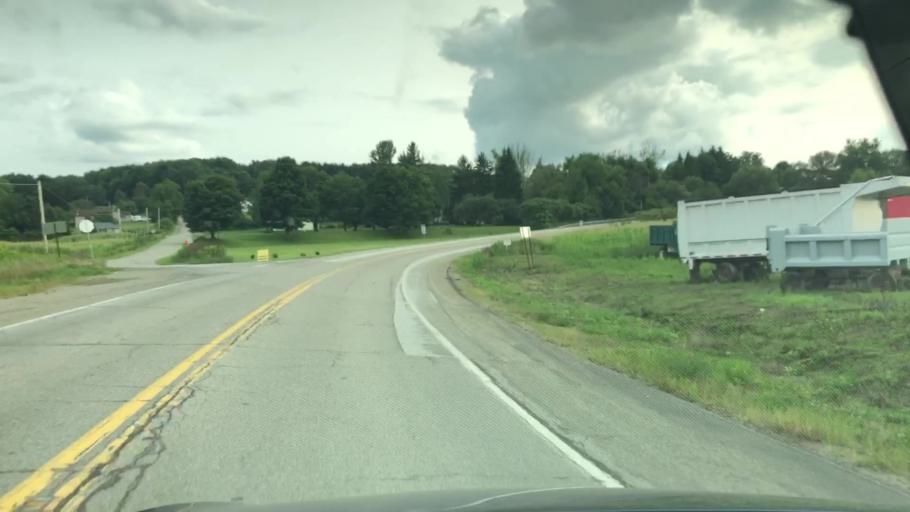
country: US
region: Pennsylvania
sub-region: Erie County
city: Union City
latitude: 41.9952
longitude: -79.8110
